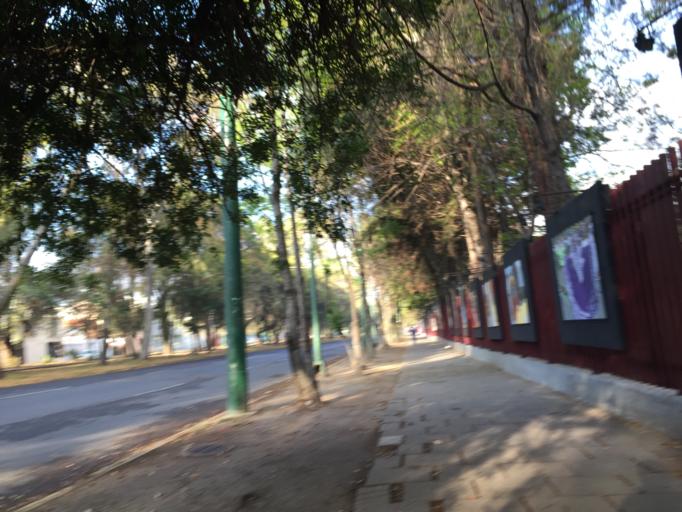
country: MX
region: Mexico
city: Colonia Lindavista
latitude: 19.4957
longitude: -99.1377
